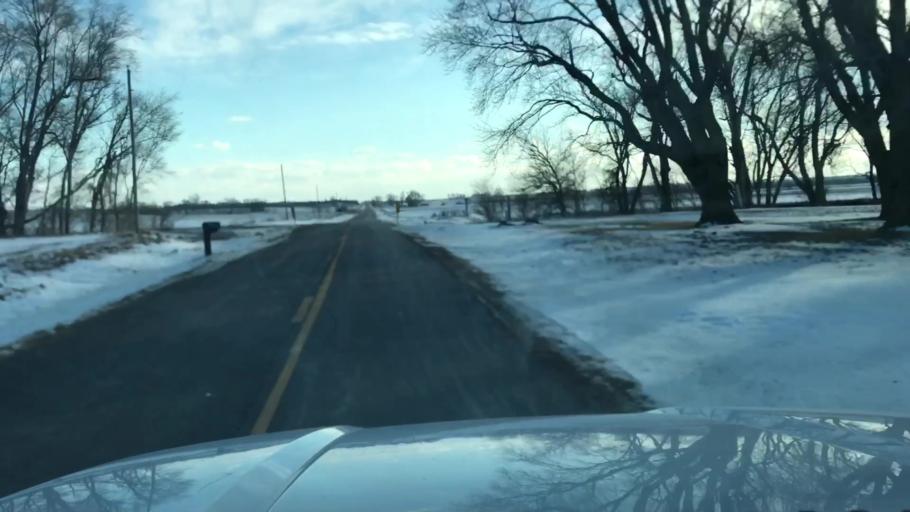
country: US
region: Missouri
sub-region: Holt County
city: Oregon
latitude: 40.1274
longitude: -95.0224
